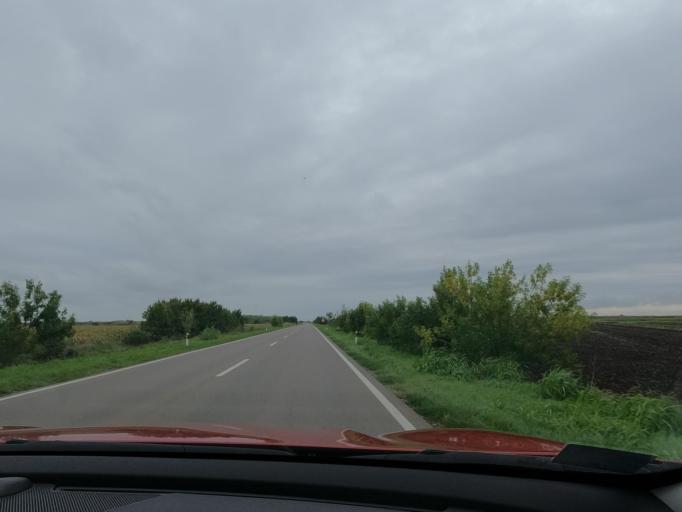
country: RS
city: Basaid
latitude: 45.6602
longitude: 20.4208
